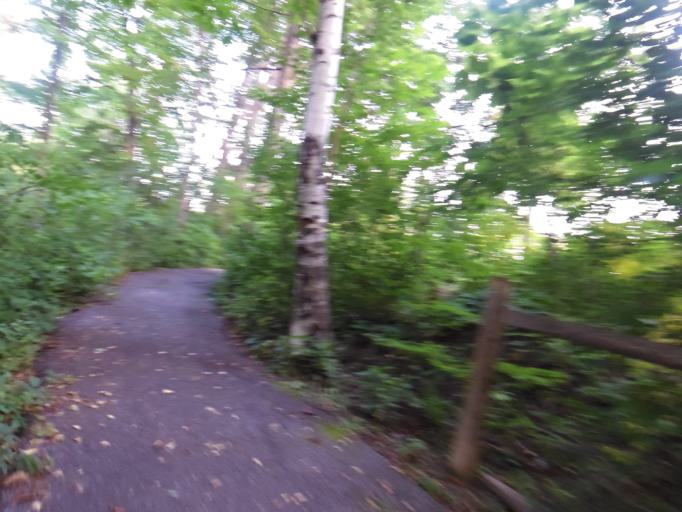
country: CA
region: Ontario
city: Bells Corners
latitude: 45.3332
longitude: -75.8012
